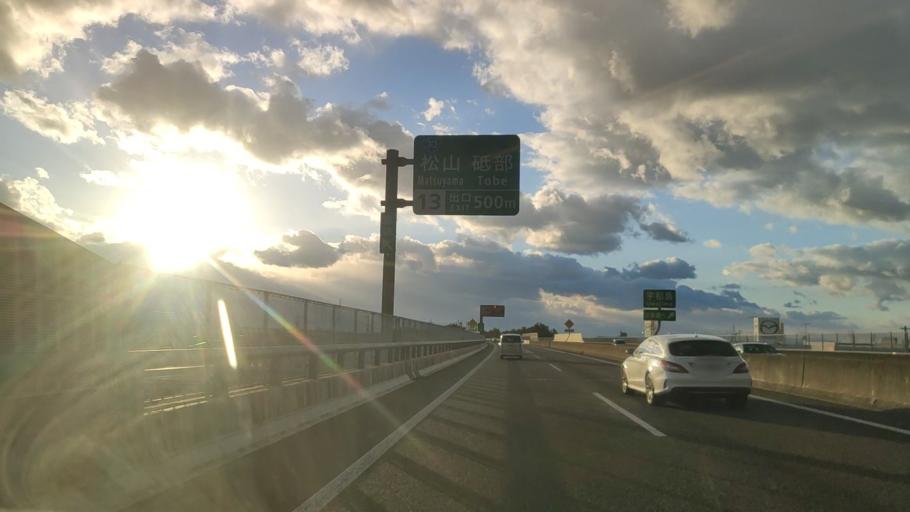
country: JP
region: Ehime
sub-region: Shikoku-chuo Shi
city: Matsuyama
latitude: 33.7965
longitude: 132.7881
